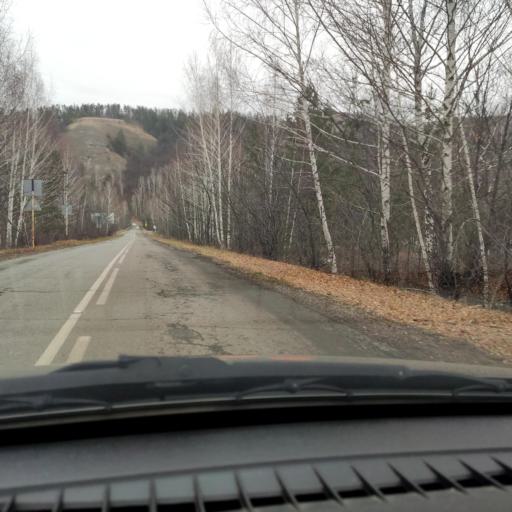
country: RU
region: Samara
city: Zhigulevsk
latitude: 53.4298
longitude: 49.6678
